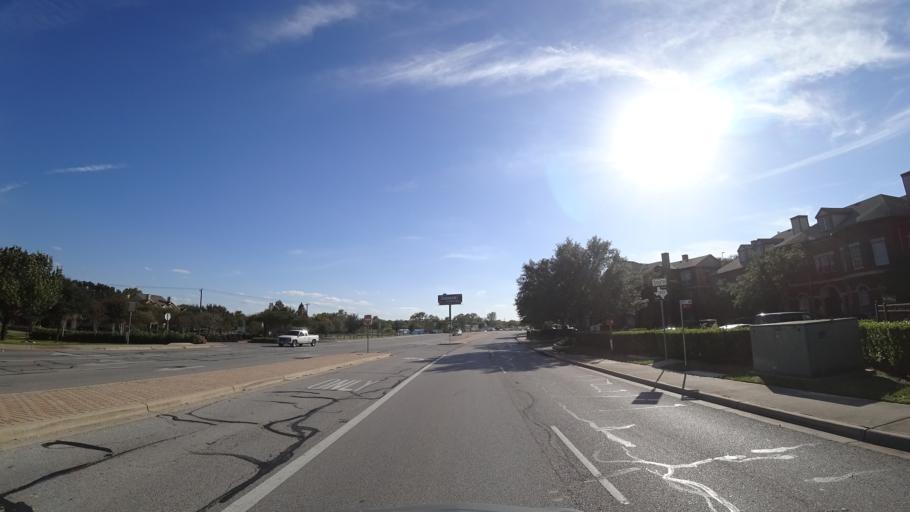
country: US
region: Texas
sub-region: Williamson County
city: Round Rock
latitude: 30.4784
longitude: -97.6853
